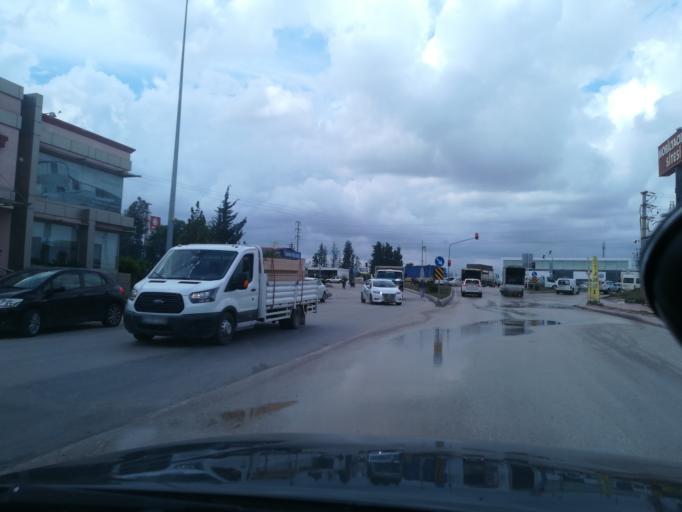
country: TR
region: Adana
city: Yuregir
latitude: 36.9824
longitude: 35.3941
